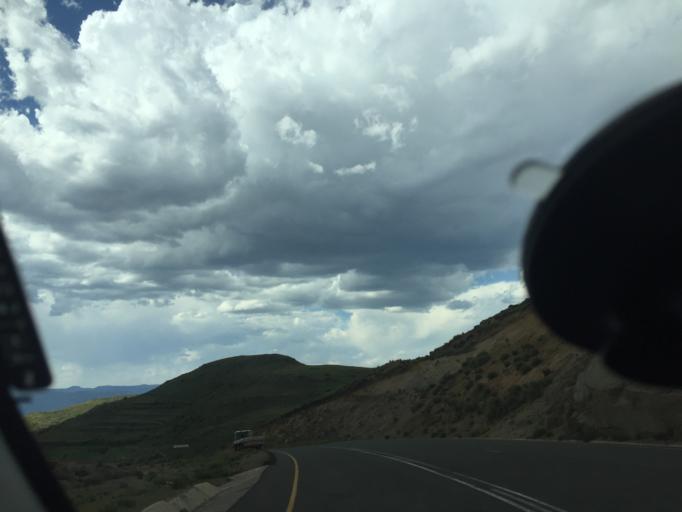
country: LS
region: Maseru
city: Nako
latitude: -29.6594
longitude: 27.9073
